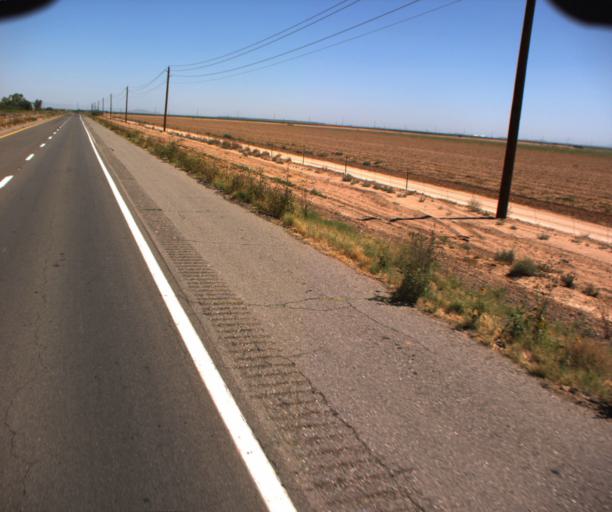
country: US
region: Arizona
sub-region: Pinal County
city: Maricopa
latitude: 32.9311
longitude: -112.0493
